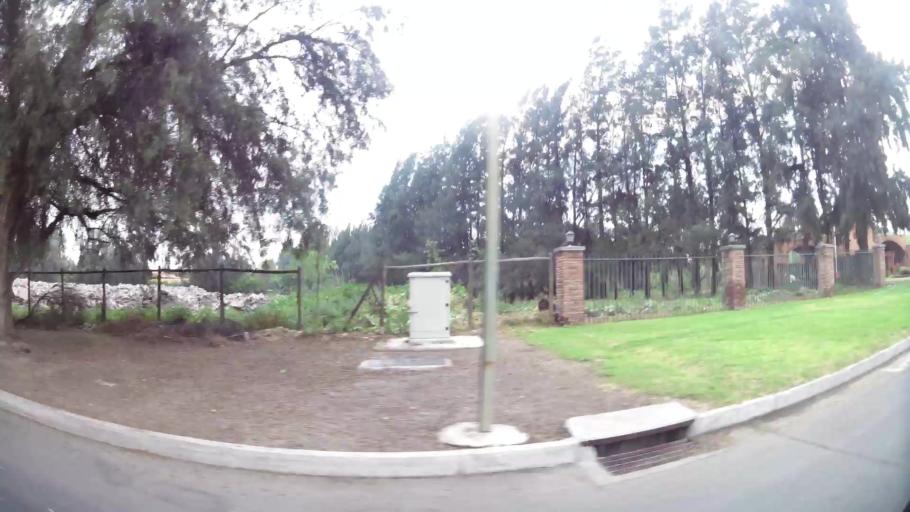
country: CL
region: Santiago Metropolitan
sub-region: Provincia de Chacabuco
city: Chicureo Abajo
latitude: -33.2766
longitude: -70.7053
